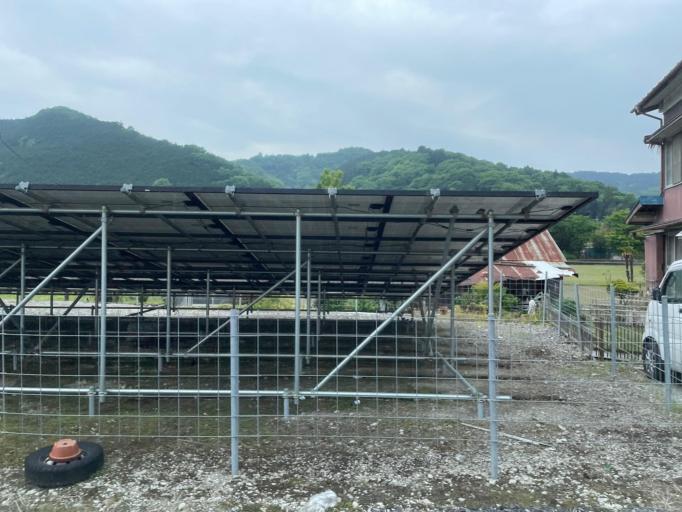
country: JP
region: Tochigi
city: Tanuma
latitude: 36.4435
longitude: 139.6494
